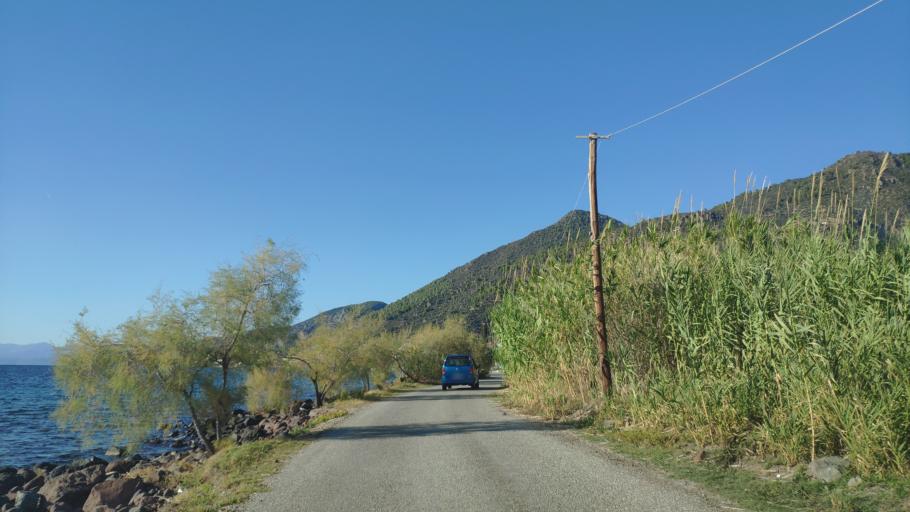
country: GR
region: Attica
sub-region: Nomos Piraios
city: Megalochori
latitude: 37.5850
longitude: 23.3486
